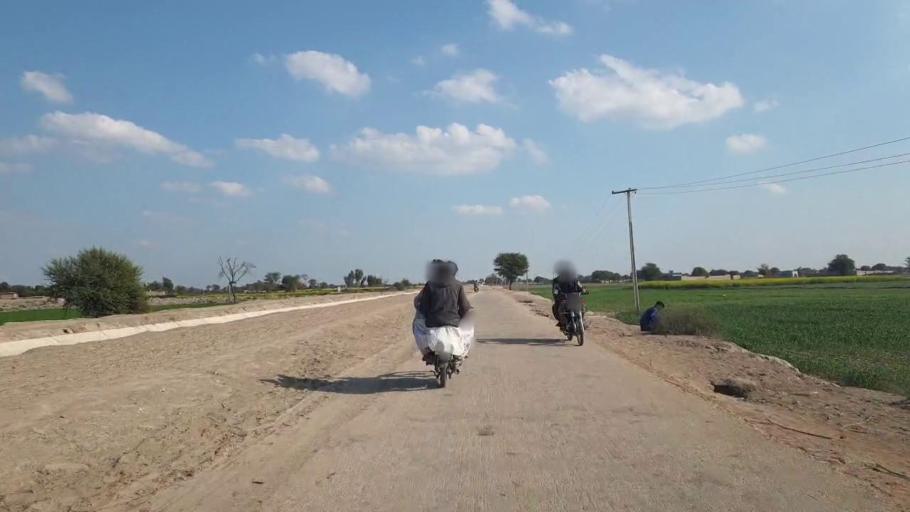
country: PK
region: Sindh
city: Shahpur Chakar
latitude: 26.1105
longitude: 68.5690
